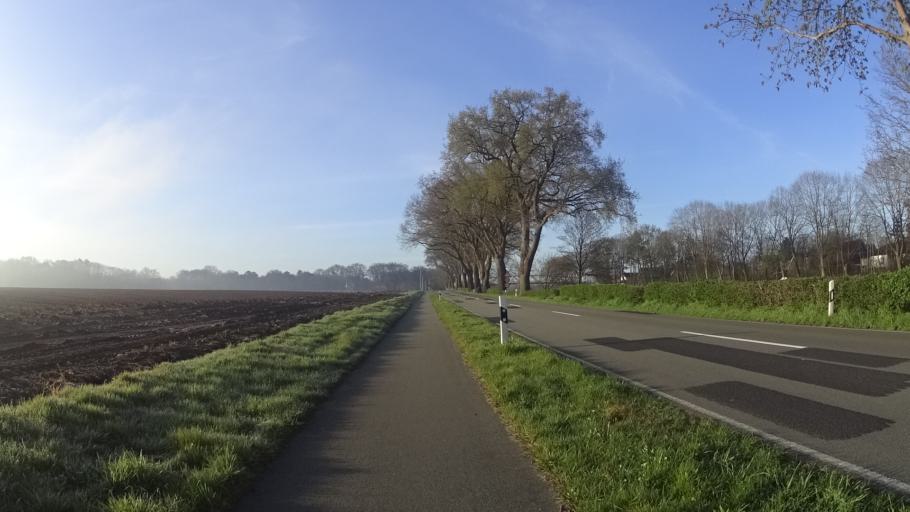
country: DE
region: Lower Saxony
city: Lathen
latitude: 52.8813
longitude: 7.3153
